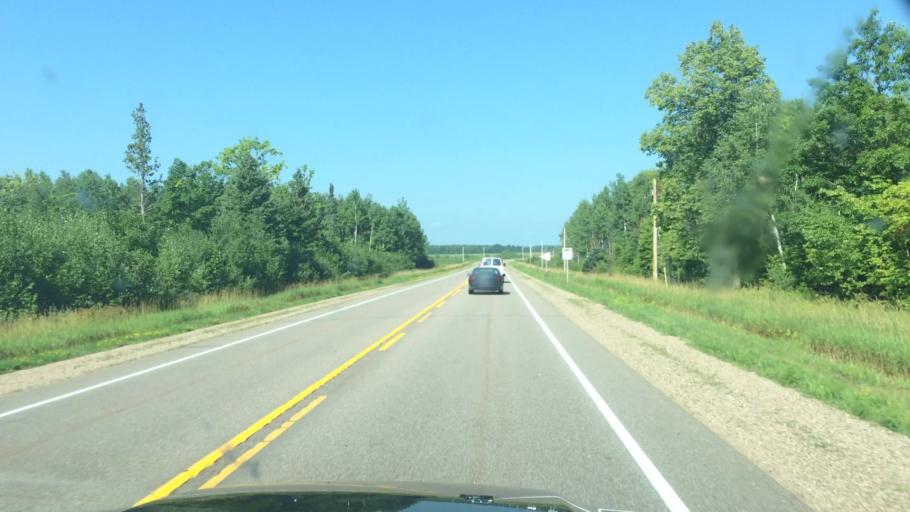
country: US
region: Wisconsin
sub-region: Langlade County
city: Antigo
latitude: 45.1470
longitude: -89.3903
